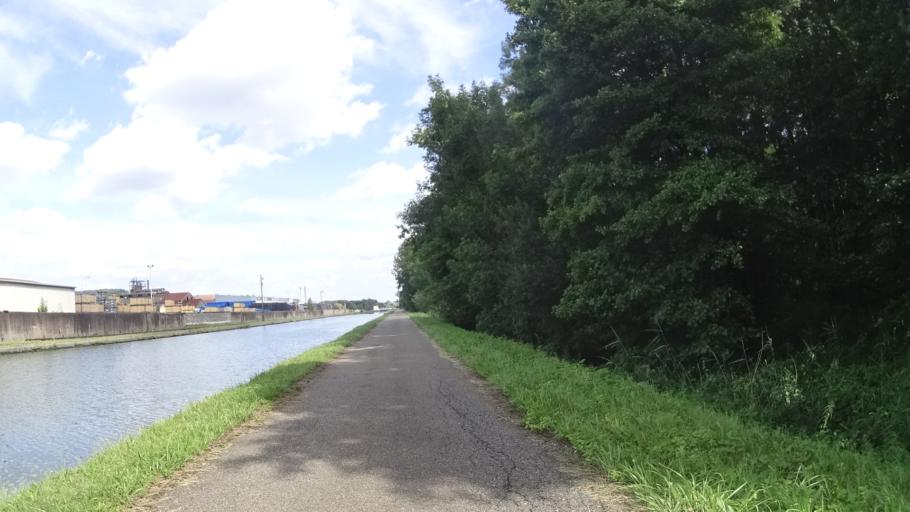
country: FR
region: Lorraine
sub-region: Departement de Meurthe-et-Moselle
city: Foug
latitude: 48.6764
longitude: 5.8024
